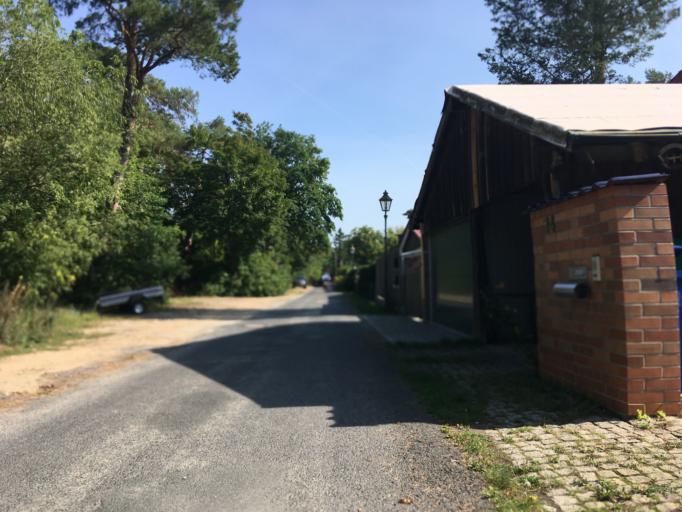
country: DE
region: Berlin
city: Schmockwitz
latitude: 52.3773
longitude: 13.6409
